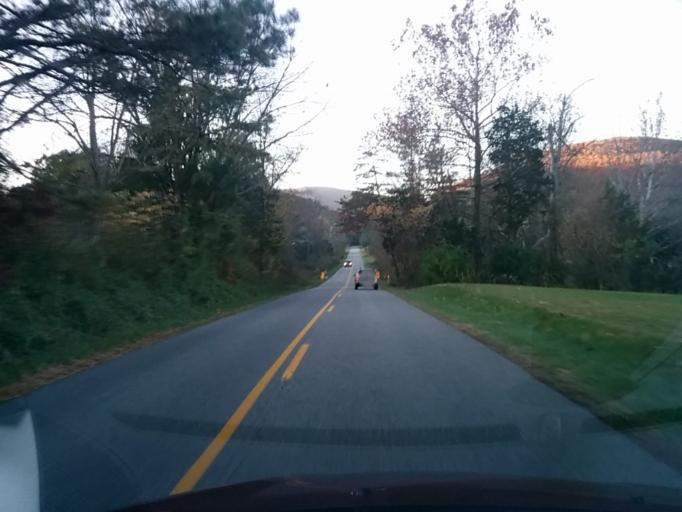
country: US
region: Virginia
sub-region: City of Lexington
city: Lexington
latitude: 37.9131
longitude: -79.5856
